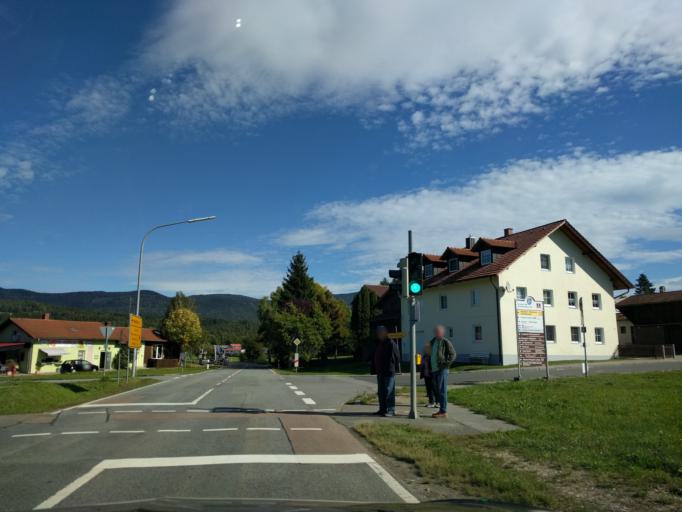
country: DE
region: Bavaria
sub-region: Upper Palatinate
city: Grafenwiesen
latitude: 49.2019
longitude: 12.8780
